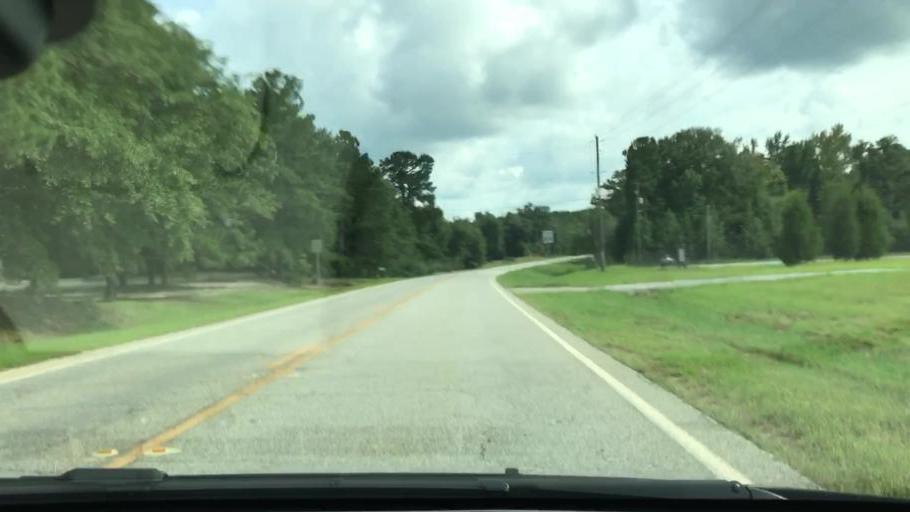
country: US
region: Georgia
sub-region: Clay County
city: Fort Gaines
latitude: 31.6471
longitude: -85.0448
